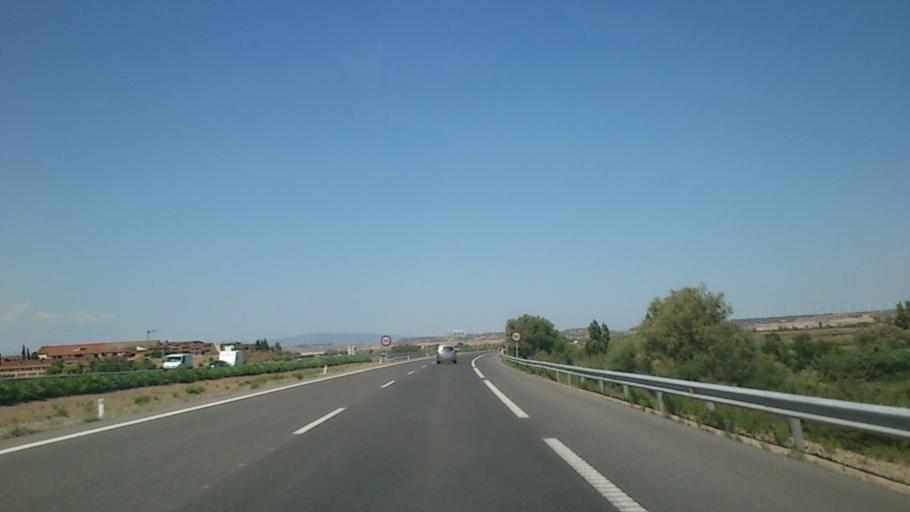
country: ES
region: Navarre
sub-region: Provincia de Navarra
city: Murchante
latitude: 42.0337
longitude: -1.6395
